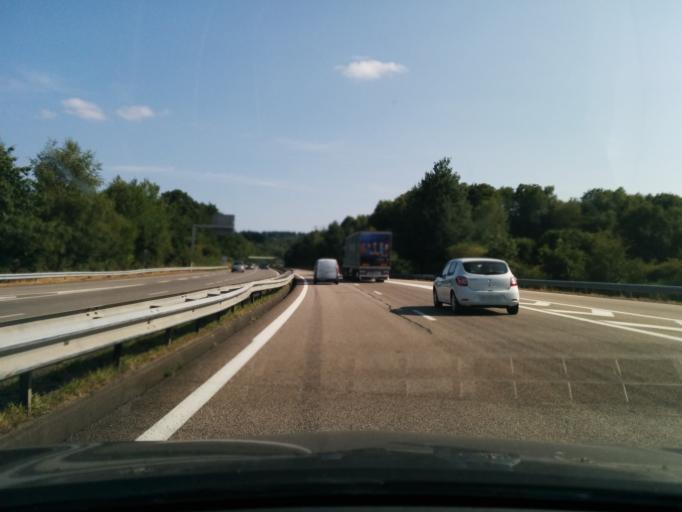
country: FR
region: Limousin
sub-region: Departement de la Haute-Vienne
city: Razes
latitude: 45.9874
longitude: 1.3249
